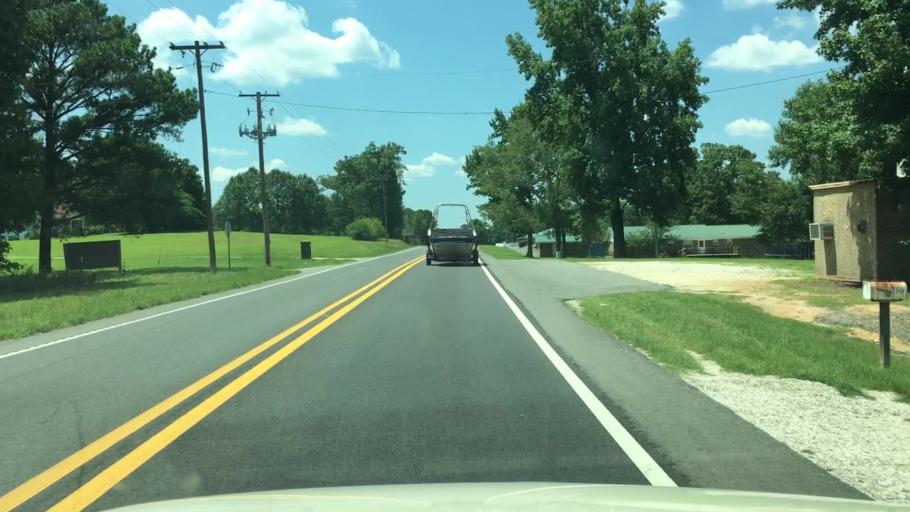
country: US
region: Arkansas
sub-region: Garland County
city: Lake Hamilton
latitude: 34.2655
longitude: -93.1374
